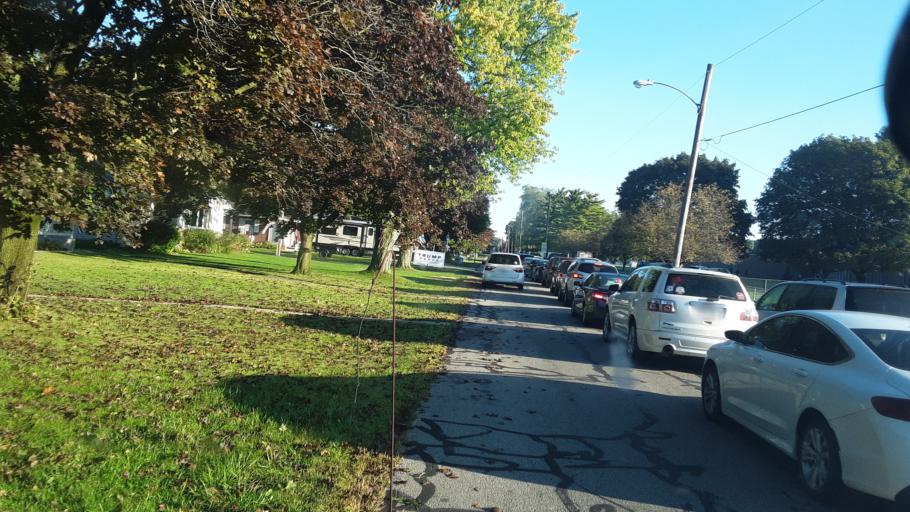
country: US
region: Ohio
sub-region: Marion County
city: Marion
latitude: 40.5826
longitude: -83.1049
